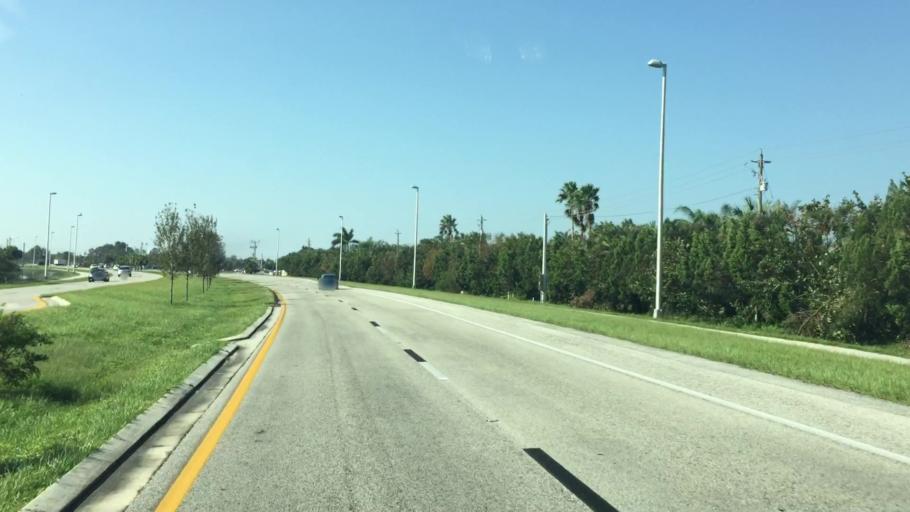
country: US
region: Florida
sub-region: Lee County
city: Villas
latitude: 26.5511
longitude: -81.8386
